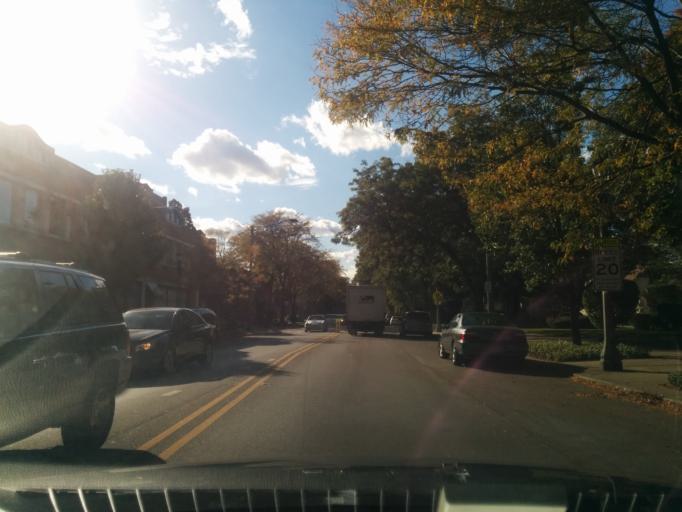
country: US
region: Illinois
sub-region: Cook County
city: Forest Park
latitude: 41.8884
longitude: -87.8154
